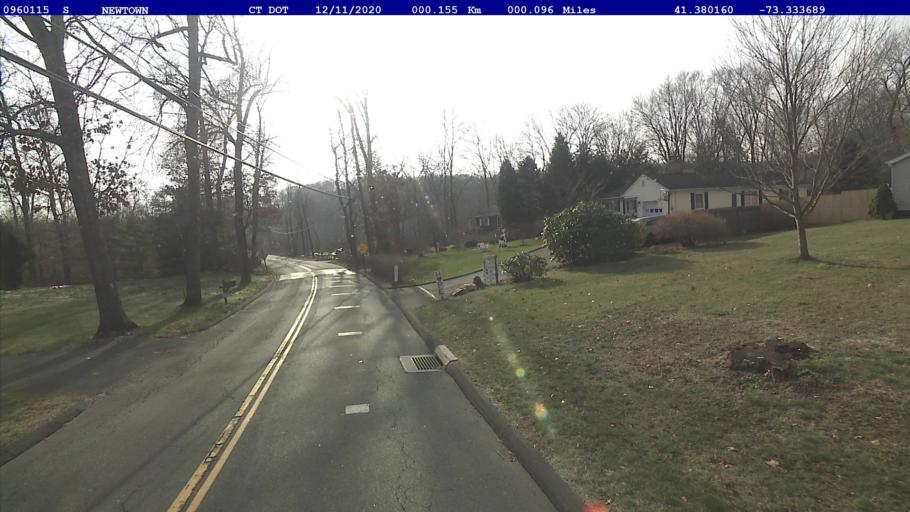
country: US
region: Connecticut
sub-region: Fairfield County
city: Newtown
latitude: 41.3801
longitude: -73.3337
